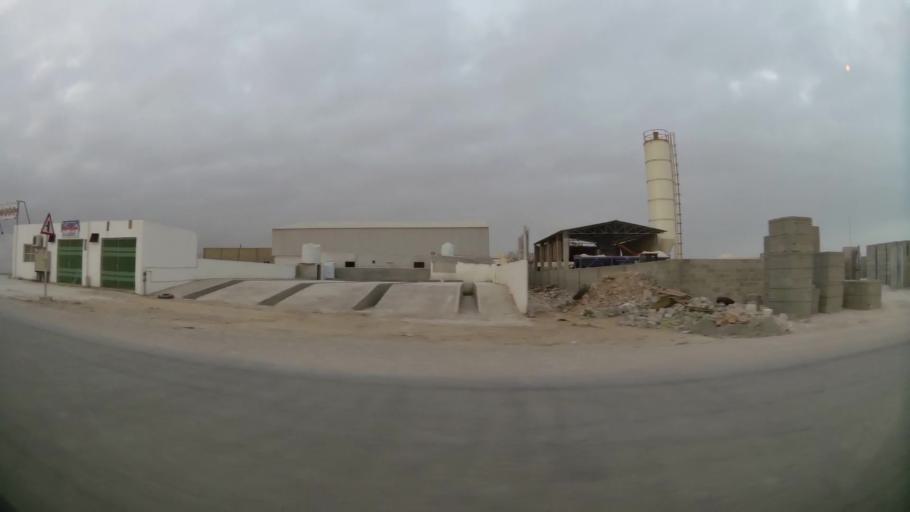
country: OM
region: Zufar
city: Salalah
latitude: 17.0268
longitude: 54.0395
